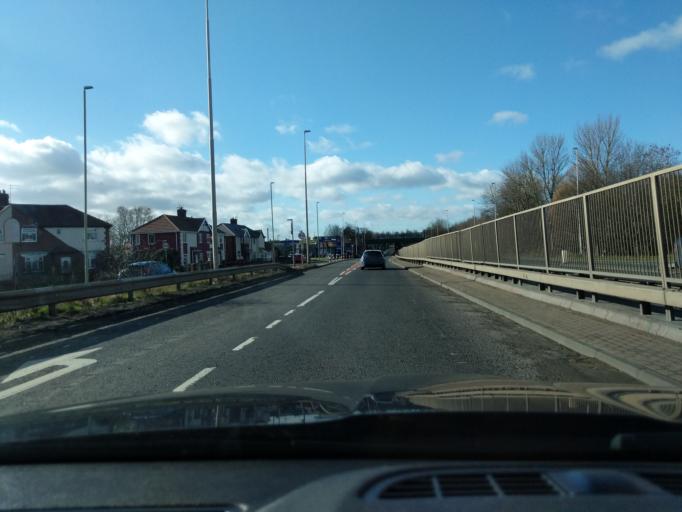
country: GB
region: England
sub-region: South Tyneside
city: Jarrow
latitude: 54.9583
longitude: -1.4919
